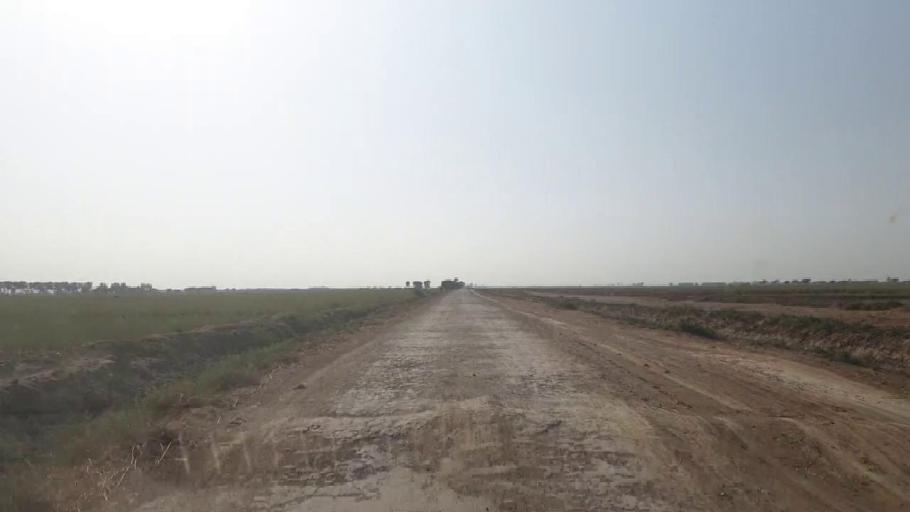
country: PK
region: Sindh
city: Kario
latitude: 24.5765
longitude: 68.5241
